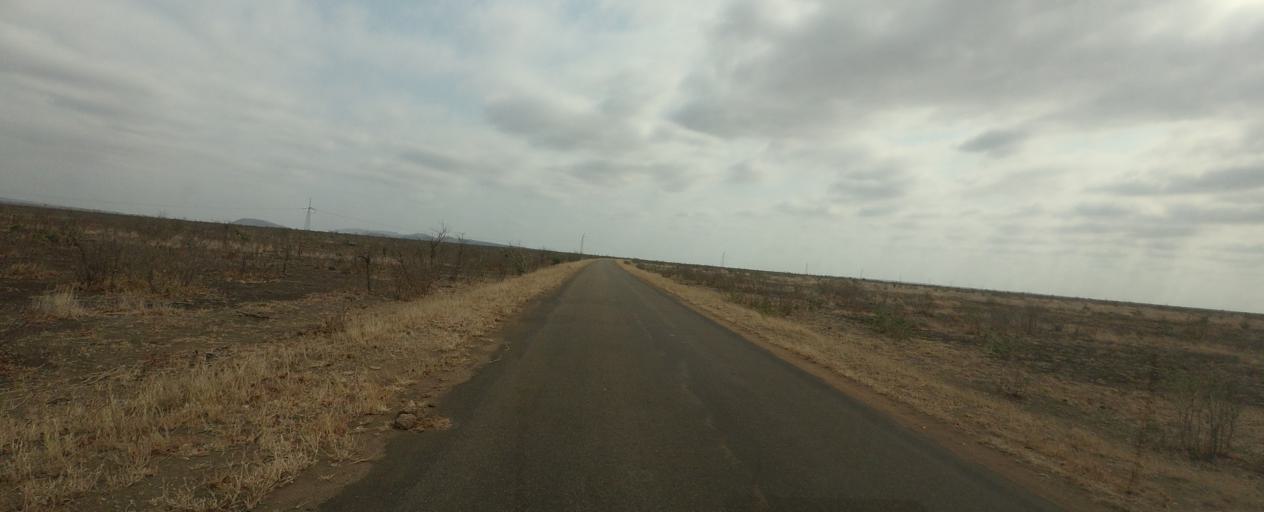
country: ZA
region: Limpopo
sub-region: Vhembe District Municipality
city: Mutale
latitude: -22.6667
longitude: 31.1677
